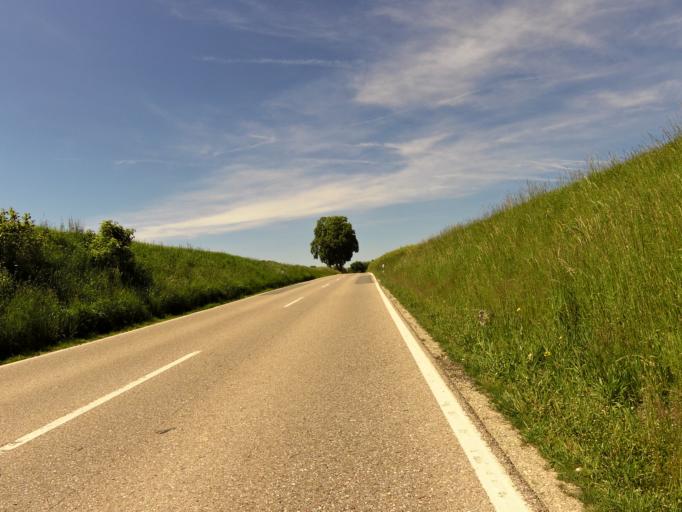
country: DE
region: Bavaria
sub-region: Upper Bavaria
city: Langenbach
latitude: 48.4680
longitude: 11.8814
